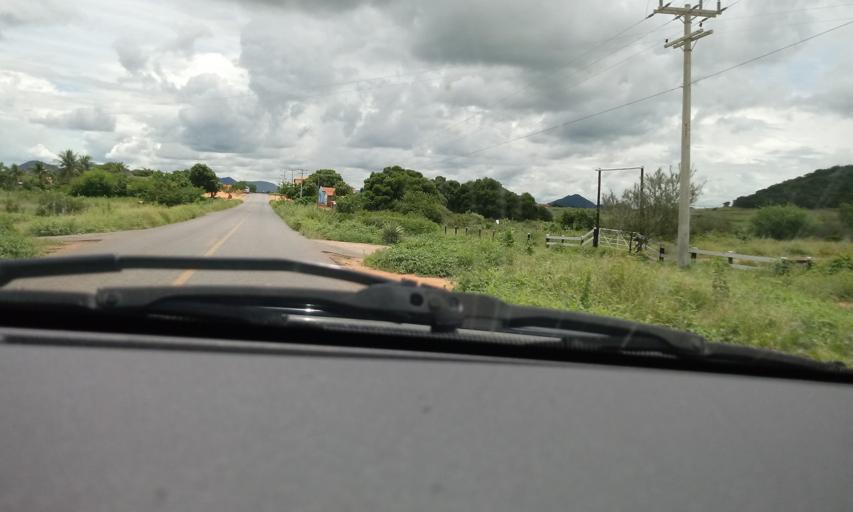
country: BR
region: Bahia
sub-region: Guanambi
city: Guanambi
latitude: -14.1160
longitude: -42.8595
